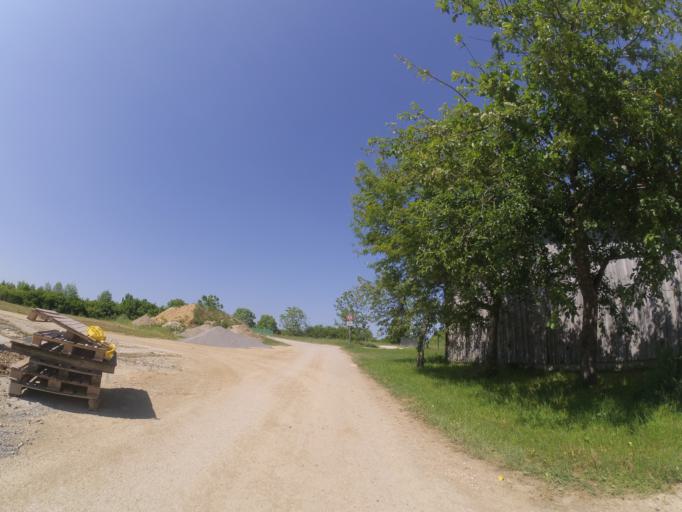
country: DE
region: Baden-Wuerttemberg
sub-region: Tuebingen Region
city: Merklingen
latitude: 48.5153
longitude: 9.7524
